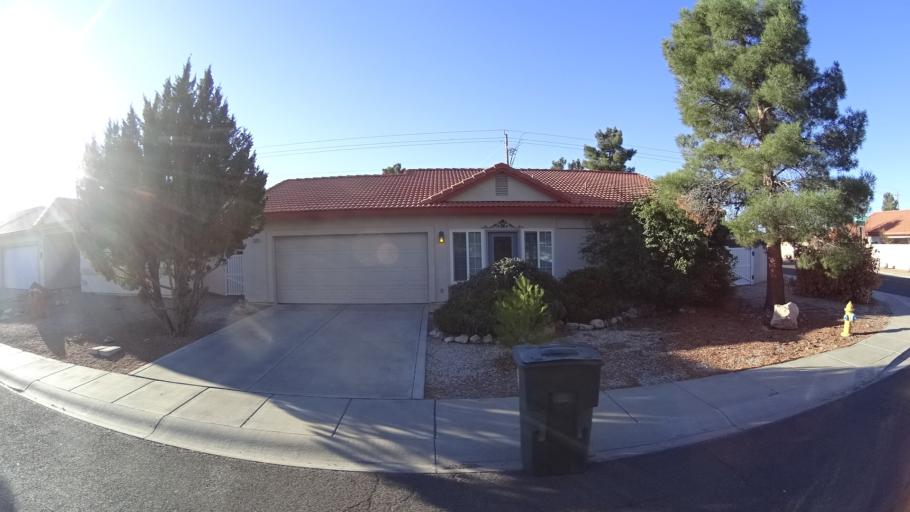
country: US
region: Arizona
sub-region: Mohave County
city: New Kingman-Butler
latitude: 35.2254
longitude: -113.9916
